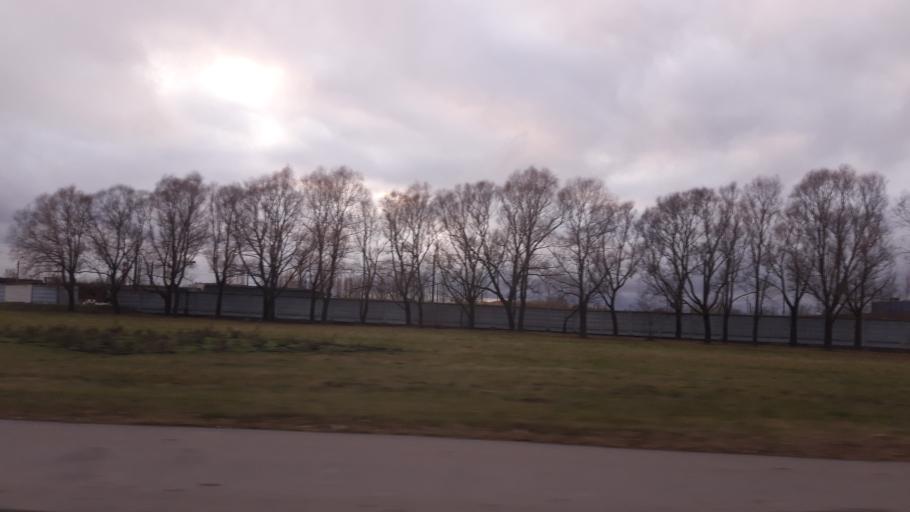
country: RU
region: St.-Petersburg
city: Kupchino
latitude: 59.8167
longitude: 30.3227
